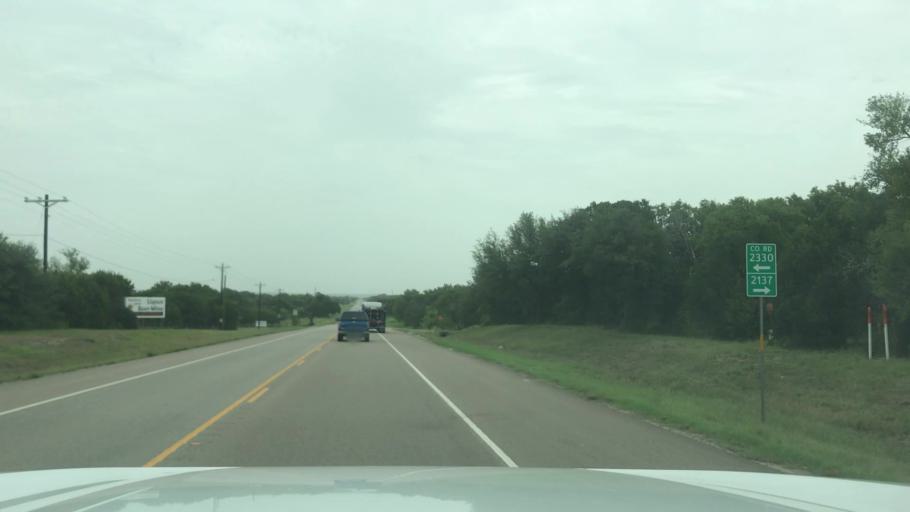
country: US
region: Texas
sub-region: Bosque County
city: Meridian
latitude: 31.9299
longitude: -97.6916
